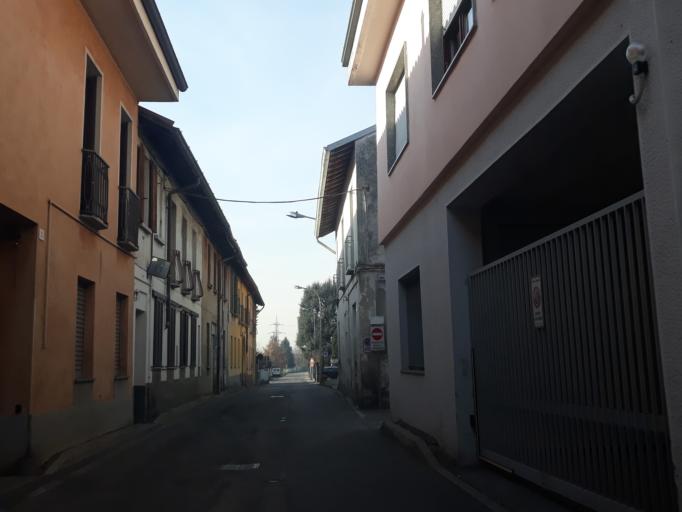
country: IT
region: Lombardy
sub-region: Provincia di Monza e Brianza
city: Bellusco
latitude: 45.6219
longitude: 9.4179
